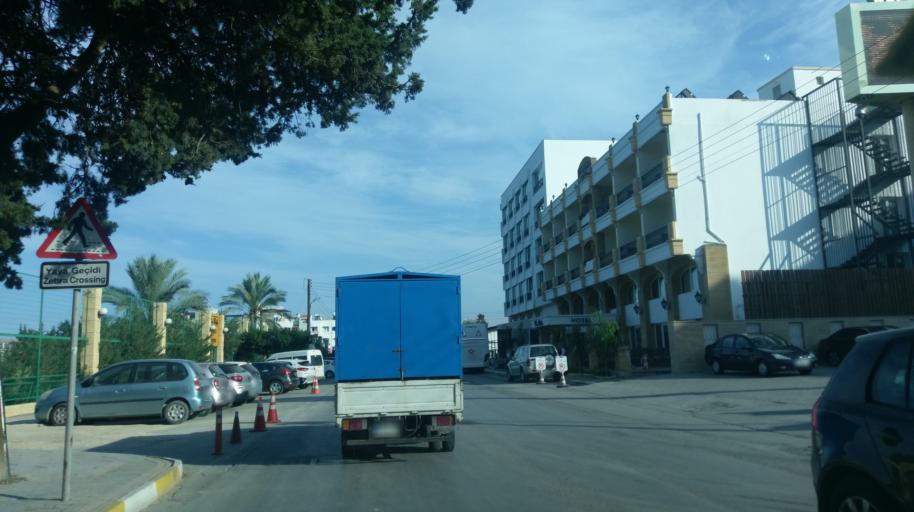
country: CY
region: Keryneia
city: Kyrenia
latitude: 35.3343
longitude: 33.3292
